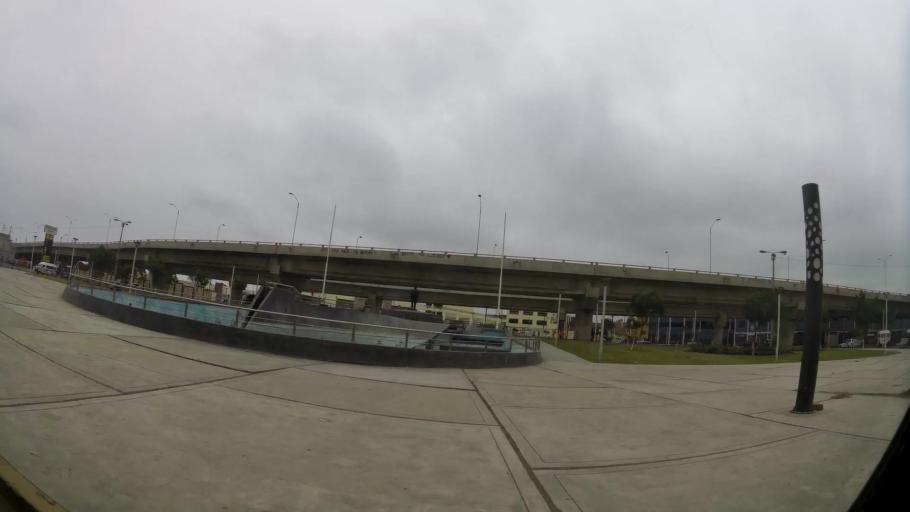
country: PE
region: La Libertad
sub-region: Provincia de Trujillo
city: Trujillo
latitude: -8.1239
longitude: -79.0227
